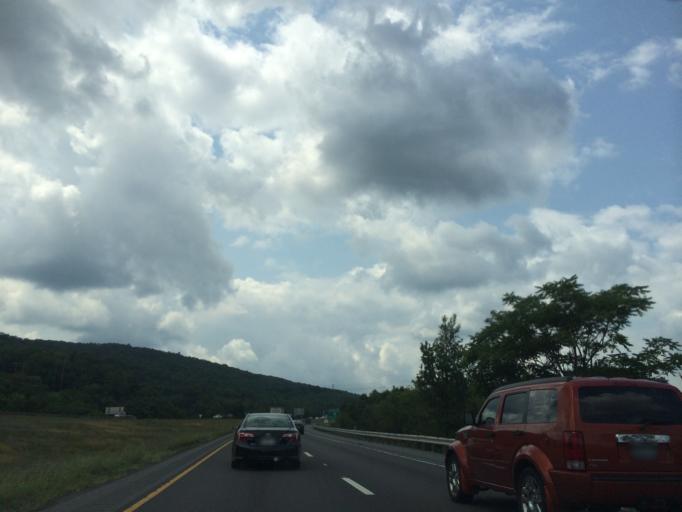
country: US
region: Pennsylvania
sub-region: Luzerne County
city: Ashley
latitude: 41.2070
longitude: -75.8999
